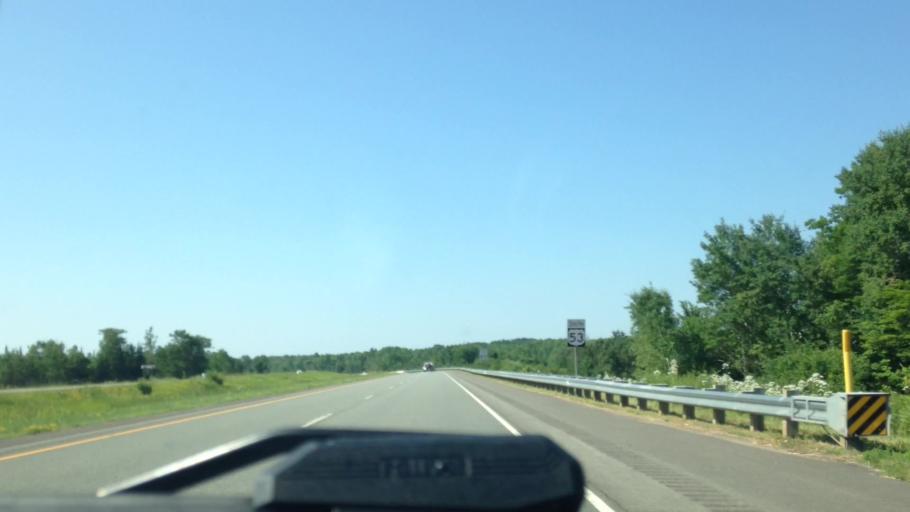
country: US
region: Wisconsin
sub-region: Douglas County
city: Lake Nebagamon
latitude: 46.4018
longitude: -91.8164
